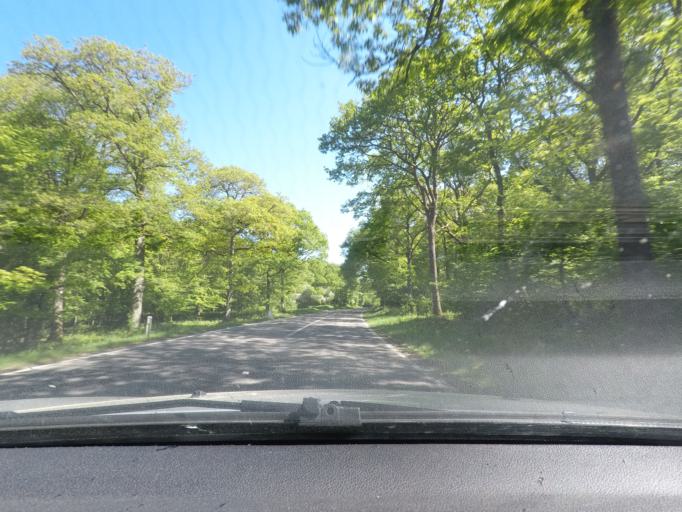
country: BE
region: Wallonia
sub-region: Province de Namur
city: Rochefort
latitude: 50.1972
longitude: 5.1307
